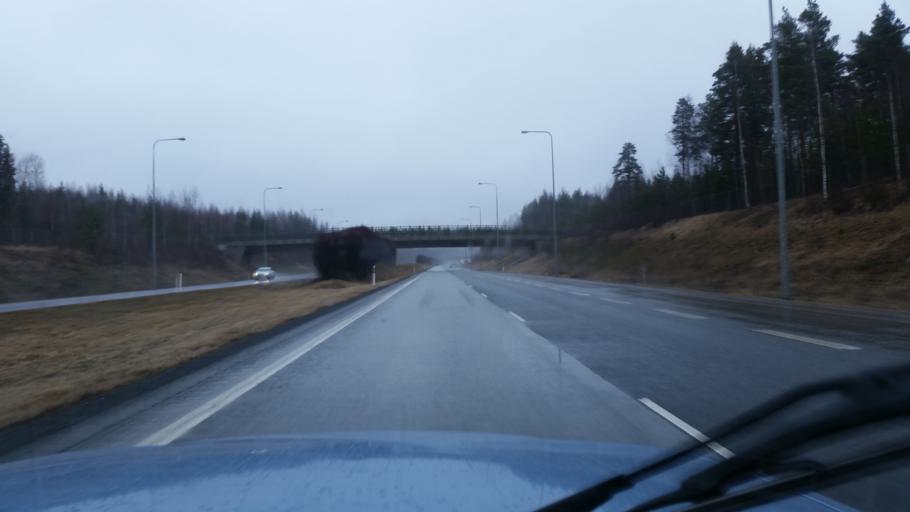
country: FI
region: Pirkanmaa
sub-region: Etelae-Pirkanmaa
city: Toijala
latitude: 61.2264
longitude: 23.8384
